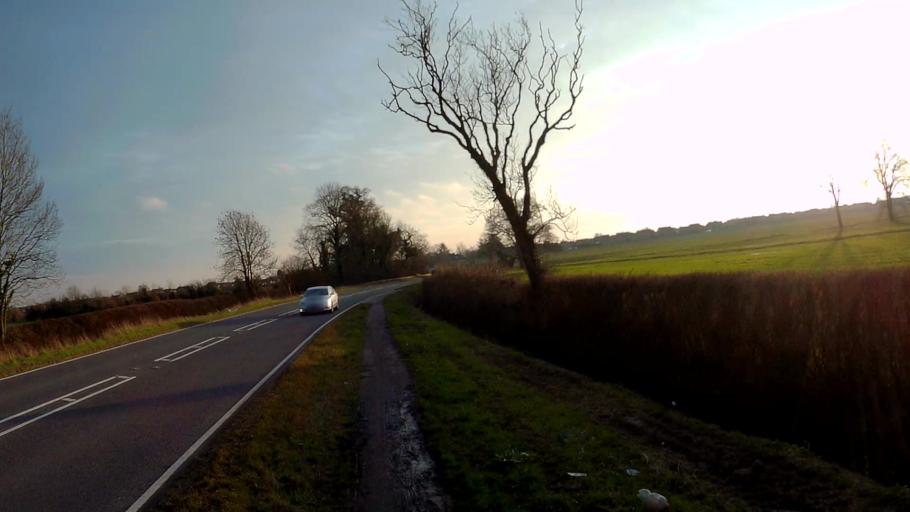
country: GB
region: England
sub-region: Lincolnshire
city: Bourne
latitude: 52.7824
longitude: -0.3770
